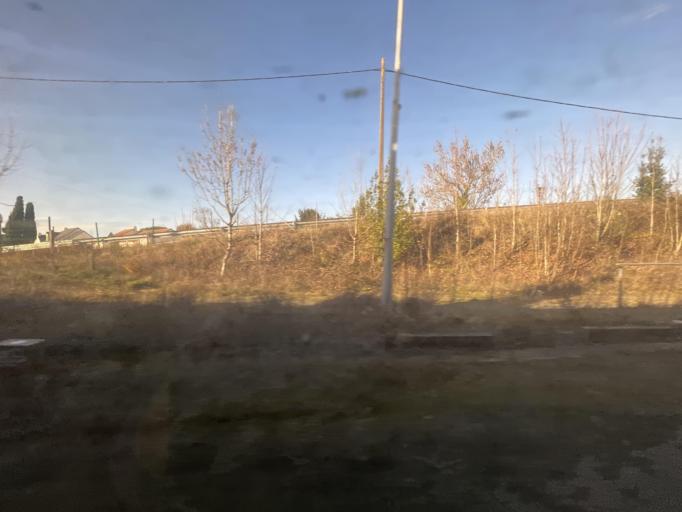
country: FR
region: Pays de la Loire
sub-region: Departement de la Loire-Atlantique
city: Sainte-Luce-sur-Loire
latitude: 47.2485
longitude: -1.4687
